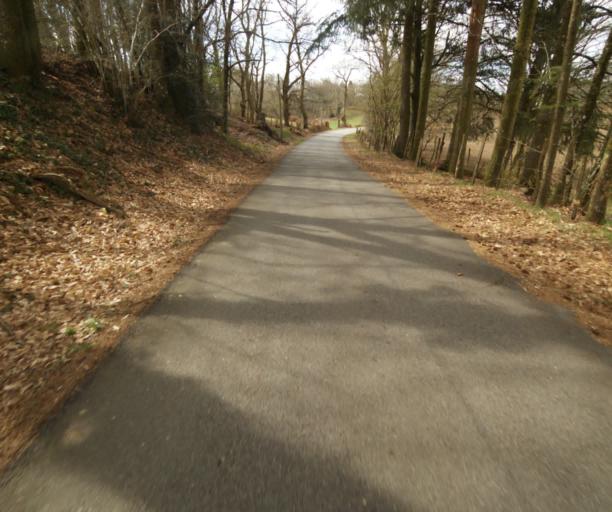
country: FR
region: Limousin
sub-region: Departement de la Correze
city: Correze
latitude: 45.3921
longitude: 1.8992
